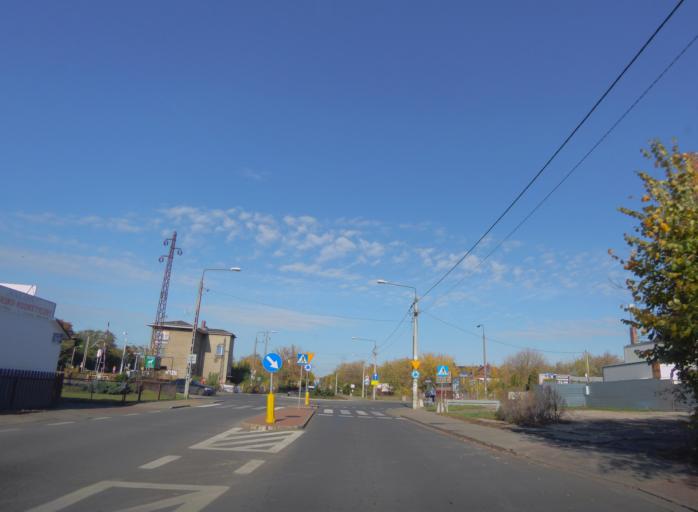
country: PL
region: Masovian Voivodeship
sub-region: Powiat otwocki
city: Jozefow
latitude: 52.1606
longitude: 21.2130
